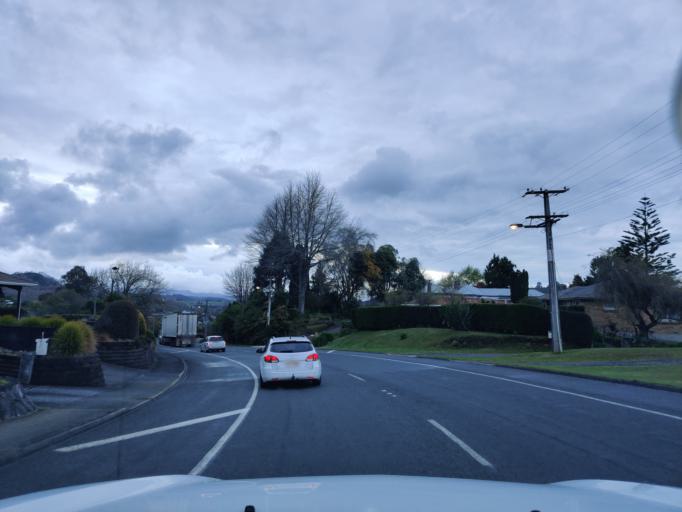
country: NZ
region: Waikato
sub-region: Otorohanga District
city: Otorohanga
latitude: -38.3444
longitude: 175.1681
